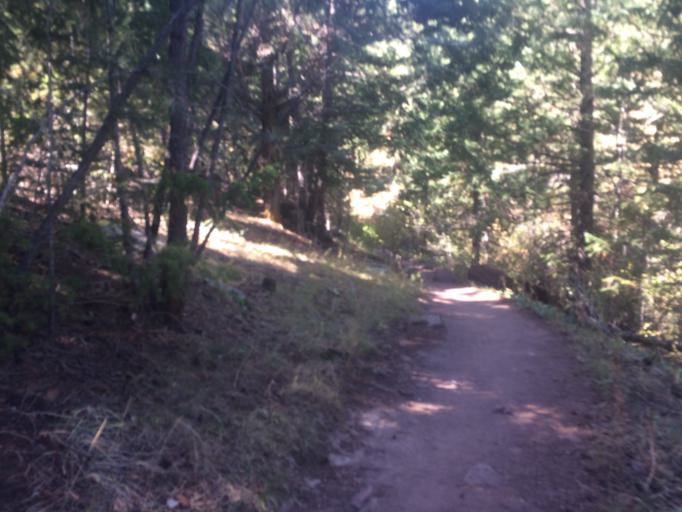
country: US
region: Colorado
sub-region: Boulder County
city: Boulder
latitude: 39.9650
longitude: -105.2800
